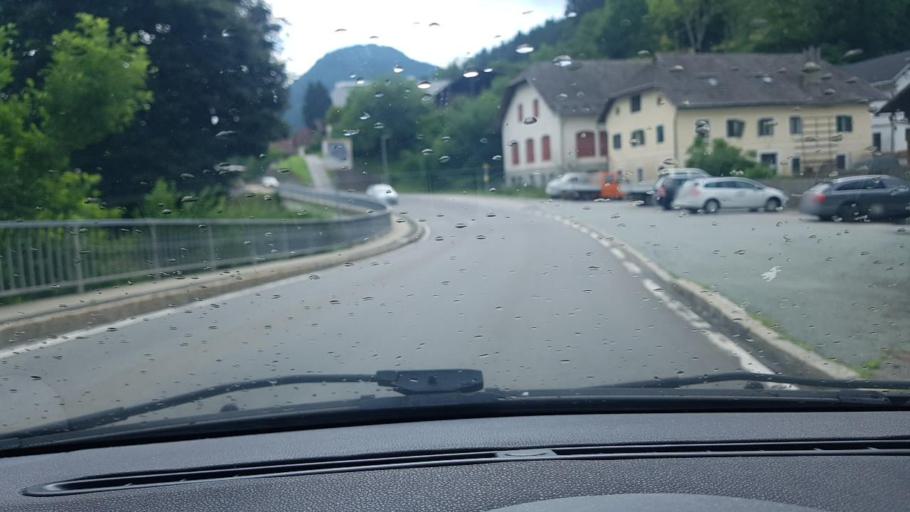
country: AT
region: Carinthia
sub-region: Politischer Bezirk Spittal an der Drau
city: Greifenburg
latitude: 46.7390
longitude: 13.2051
